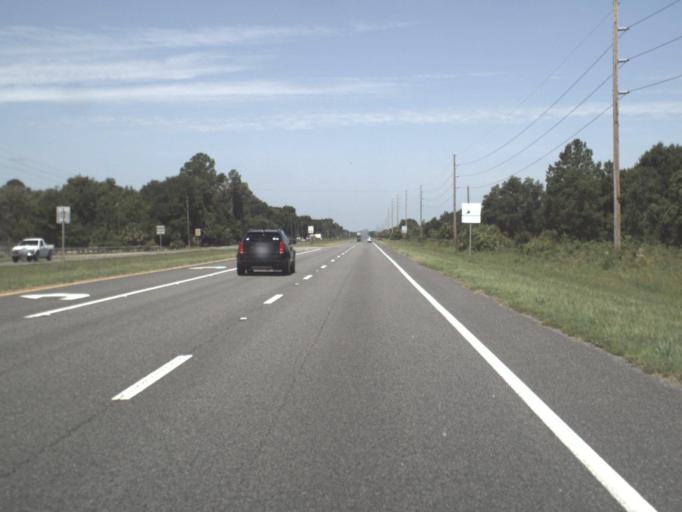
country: US
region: Florida
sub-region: Dixie County
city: Cross City
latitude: 29.6073
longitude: -83.0567
